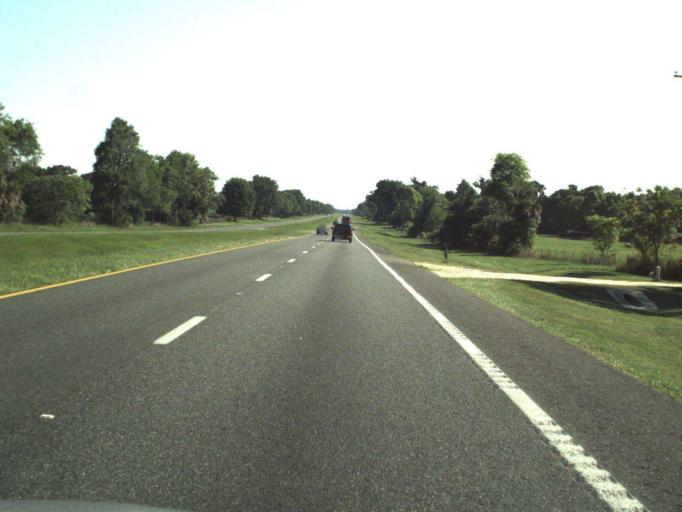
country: US
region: Florida
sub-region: Marion County
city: Citra
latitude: 29.3488
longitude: -82.1458
